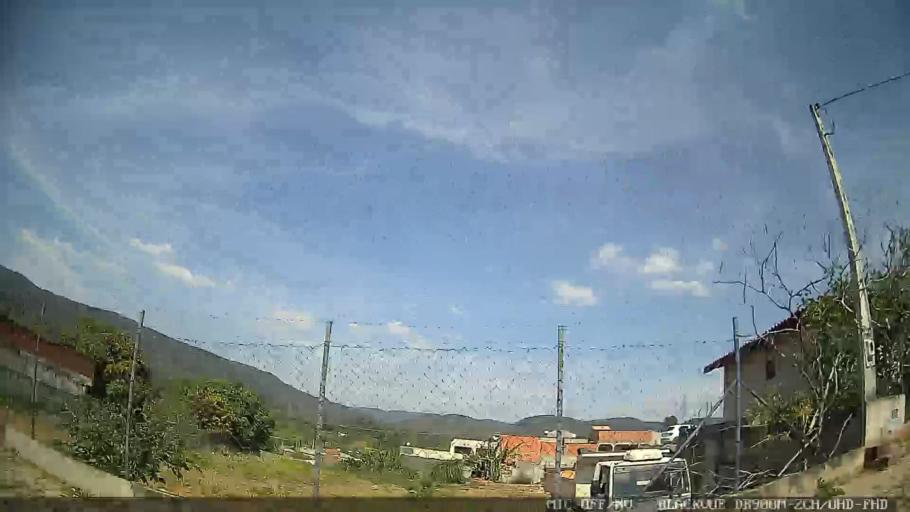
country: BR
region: Sao Paulo
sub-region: Cabreuva
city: Cabreuva
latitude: -23.2722
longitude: -47.0522
